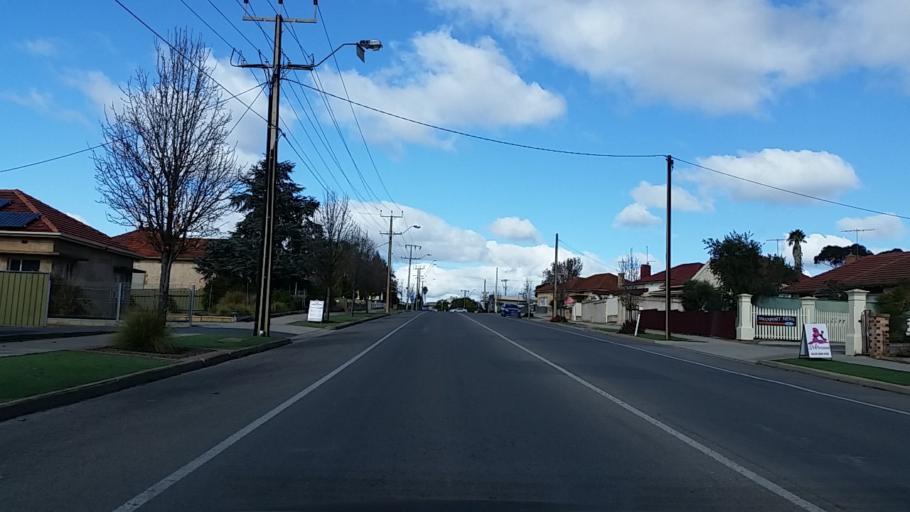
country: AU
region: South Australia
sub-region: Murray Bridge
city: Murray Bridge
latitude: -35.1270
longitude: 139.2784
